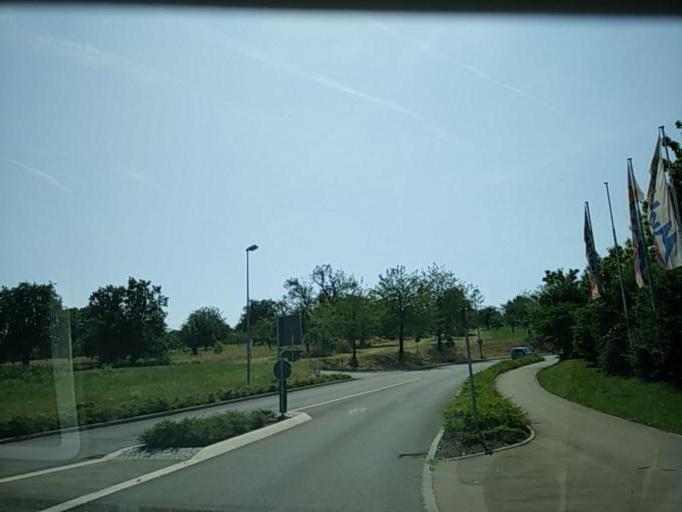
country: DE
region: Baden-Wuerttemberg
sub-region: Tuebingen Region
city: Gomaringen
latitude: 48.4615
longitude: 9.1053
